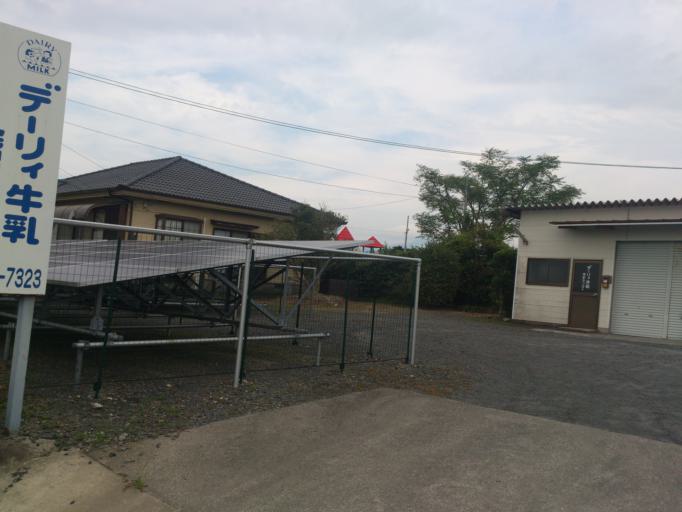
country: JP
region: Kagoshima
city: Kanoya
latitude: 31.3604
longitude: 130.9243
